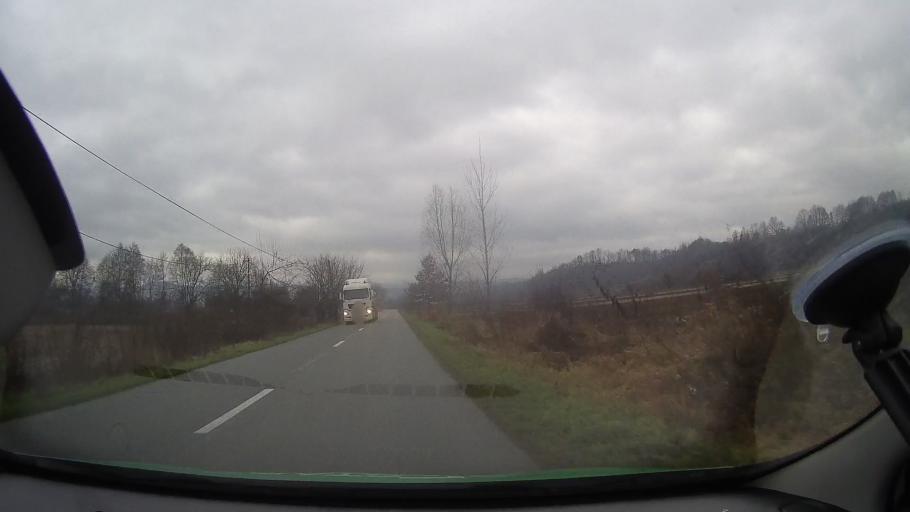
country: RO
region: Arad
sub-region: Comuna Gurahont
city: Gurahont
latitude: 46.2581
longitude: 22.3358
